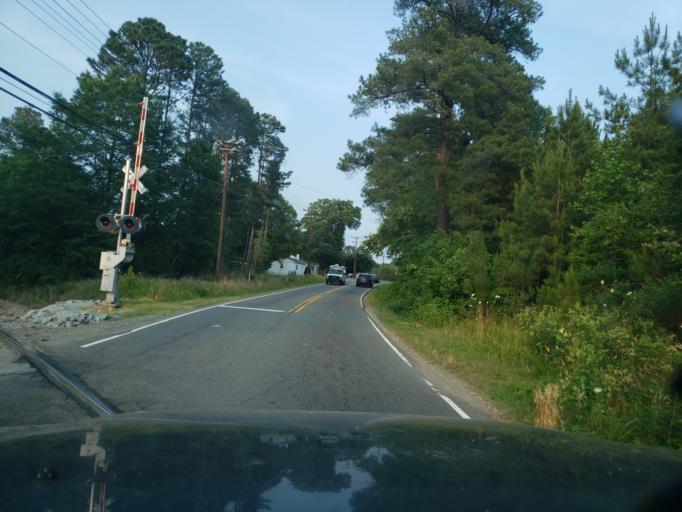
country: US
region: North Carolina
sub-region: Durham County
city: Durham
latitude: 35.9578
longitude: -78.8774
